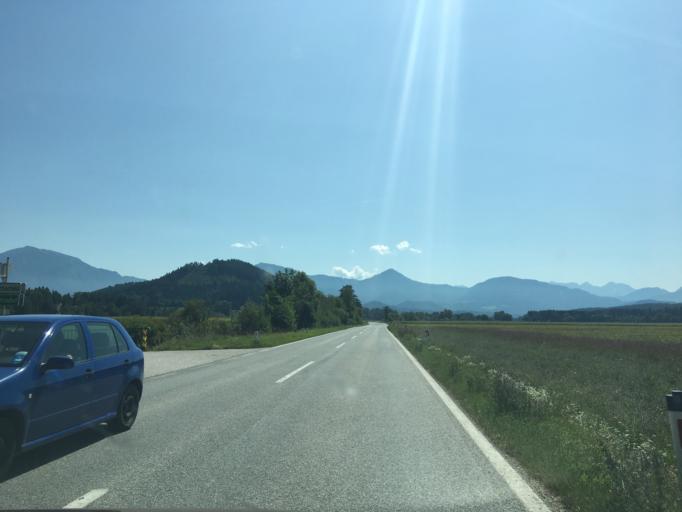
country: AT
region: Carinthia
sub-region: Politischer Bezirk Volkermarkt
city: Eberndorf
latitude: 46.6173
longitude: 14.6354
